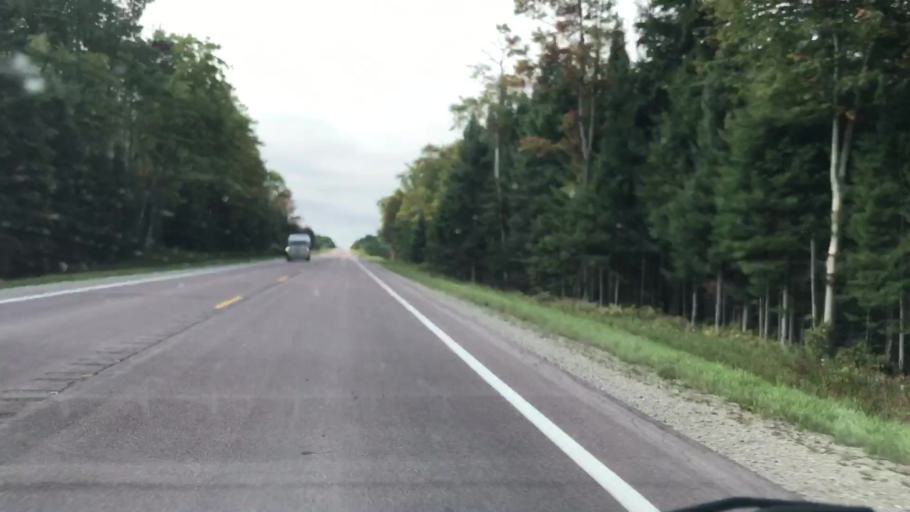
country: US
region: Michigan
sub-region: Luce County
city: Newberry
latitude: 46.2916
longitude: -85.5697
